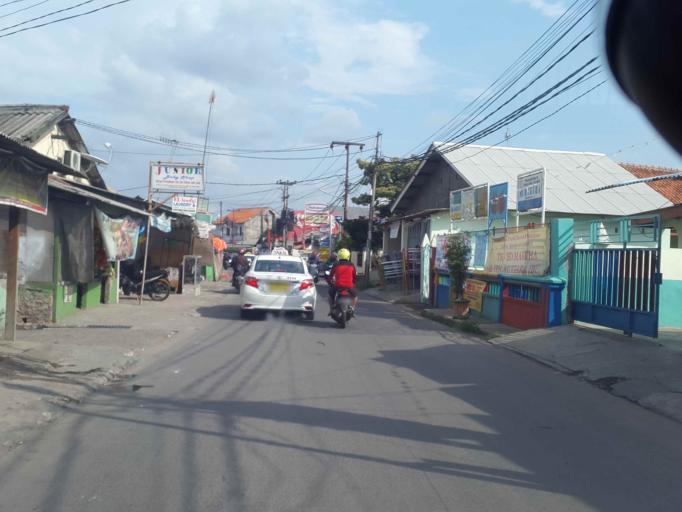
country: ID
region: West Java
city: Bekasi
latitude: -6.2776
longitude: 106.9185
